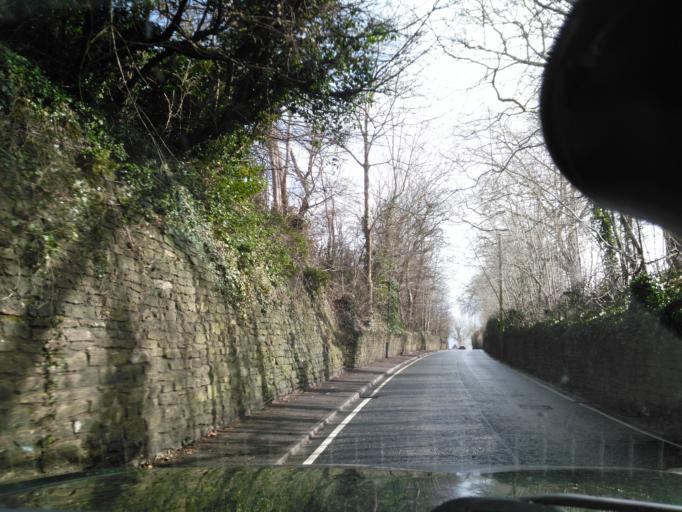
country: GB
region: England
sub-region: Wiltshire
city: Bradford-on-Avon
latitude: 51.3470
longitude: -2.2419
